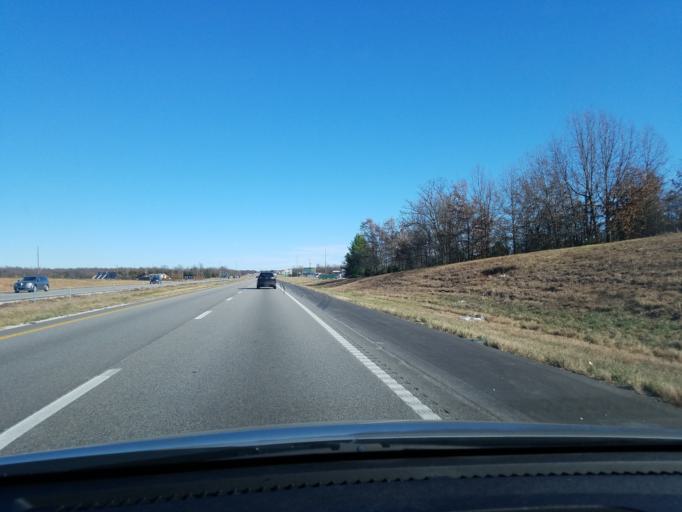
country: US
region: Missouri
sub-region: Greene County
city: Strafford
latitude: 37.2530
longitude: -93.1748
